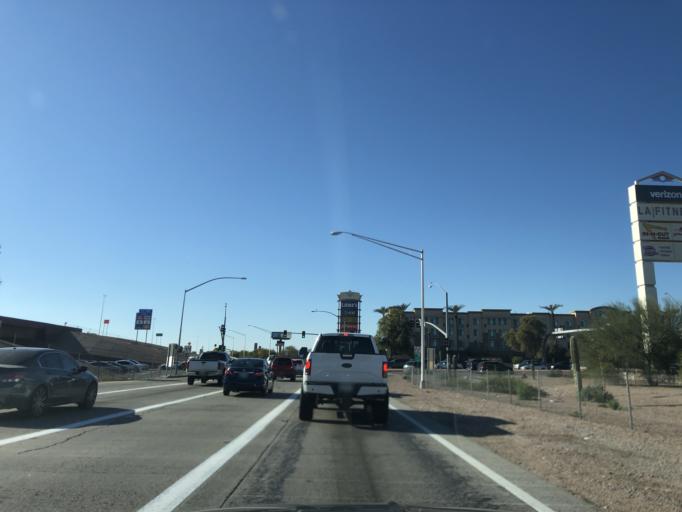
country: US
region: Arizona
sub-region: Maricopa County
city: Avondale
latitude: 33.4585
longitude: -112.3401
